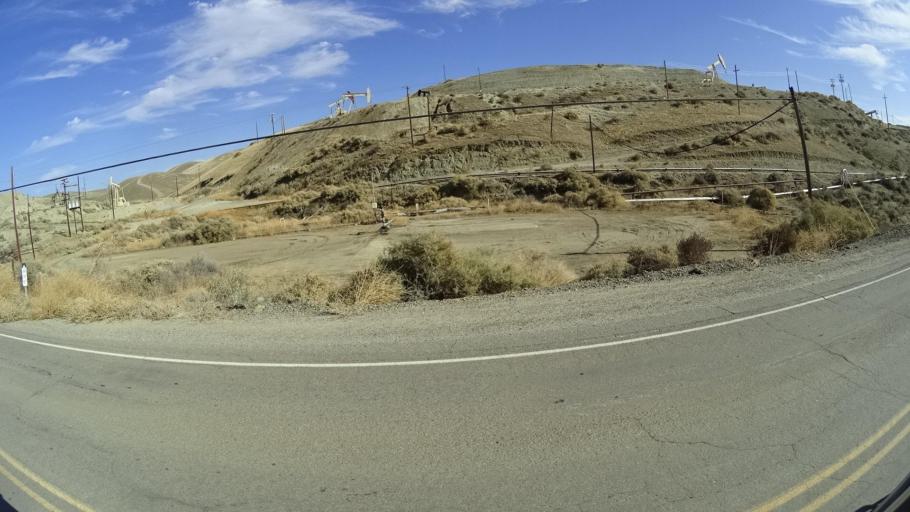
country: US
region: California
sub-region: Kern County
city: Oildale
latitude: 35.5854
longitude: -118.9589
